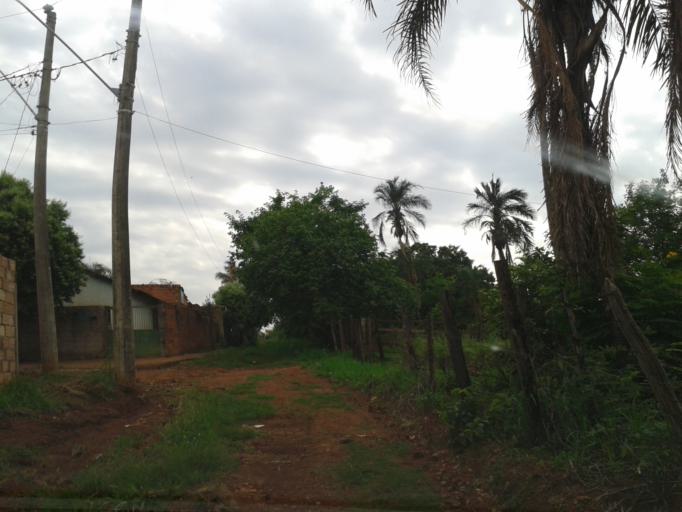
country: BR
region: Minas Gerais
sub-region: Ituiutaba
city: Ituiutaba
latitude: -18.9783
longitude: -49.4439
